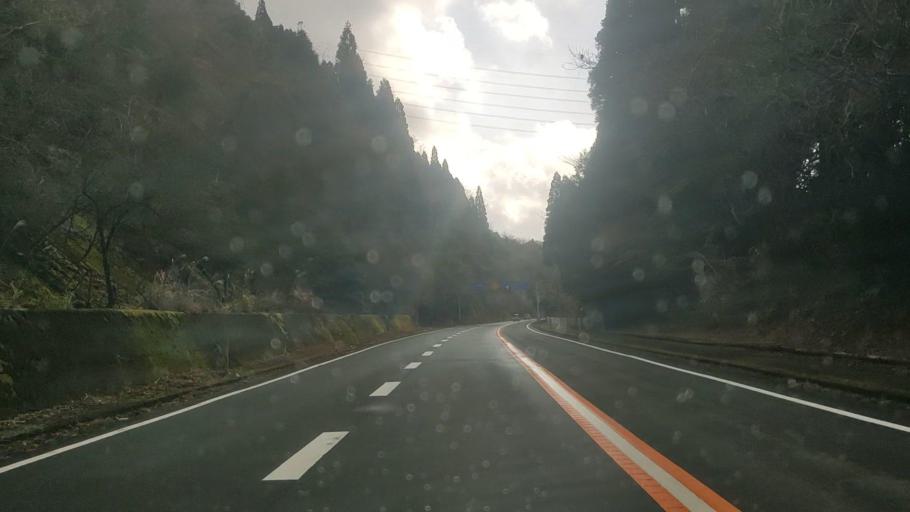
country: JP
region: Kumamoto
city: Hitoyoshi
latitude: 32.1115
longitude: 130.8055
